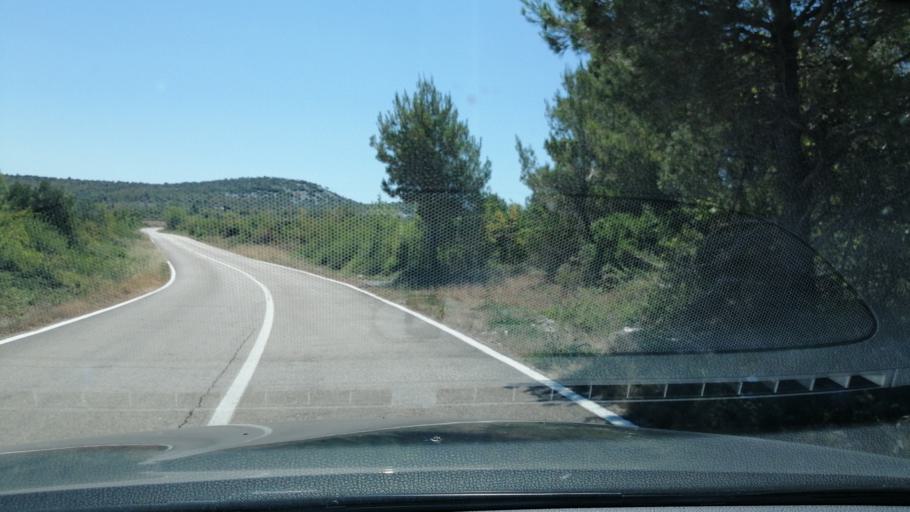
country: HR
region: Sibensko-Kniniska
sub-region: Grad Sibenik
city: Pirovac
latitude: 43.8619
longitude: 15.6899
